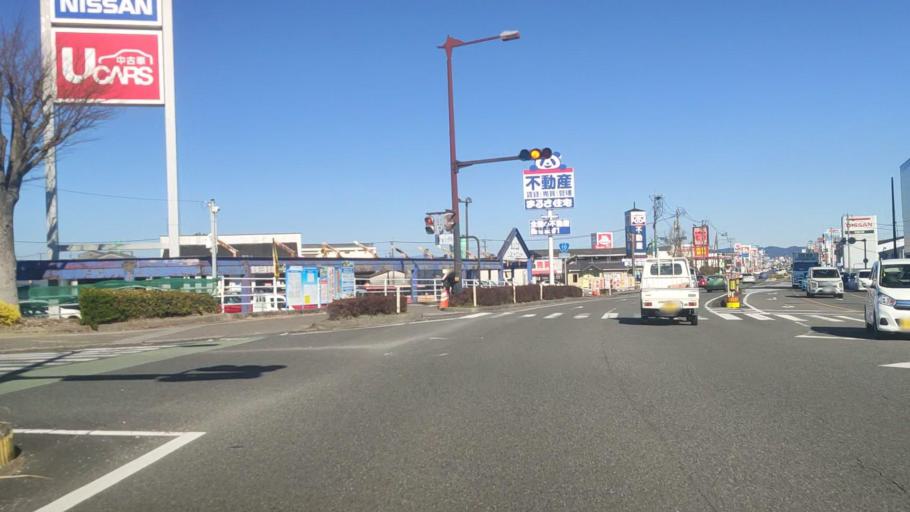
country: JP
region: Miyazaki
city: Miyakonojo
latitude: 31.7514
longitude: 131.0781
